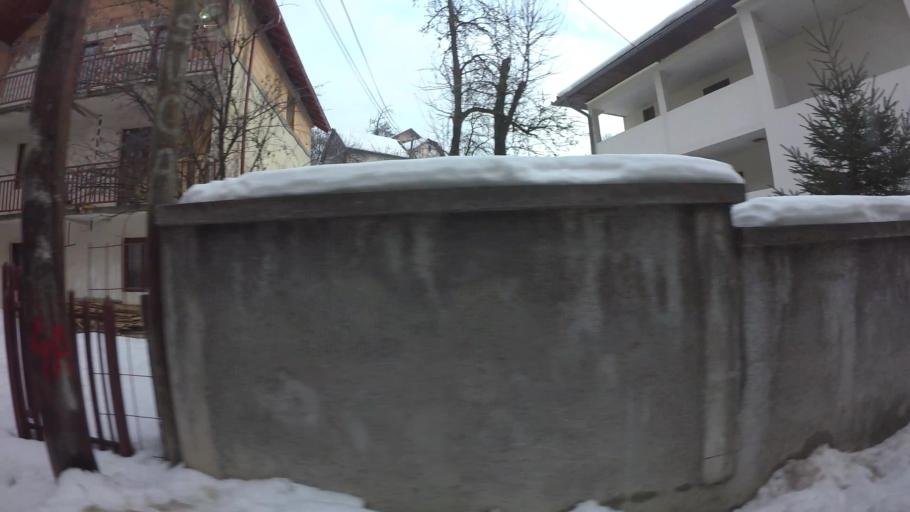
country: BA
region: Federation of Bosnia and Herzegovina
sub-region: Kanton Sarajevo
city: Sarajevo
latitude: 43.8602
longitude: 18.3493
